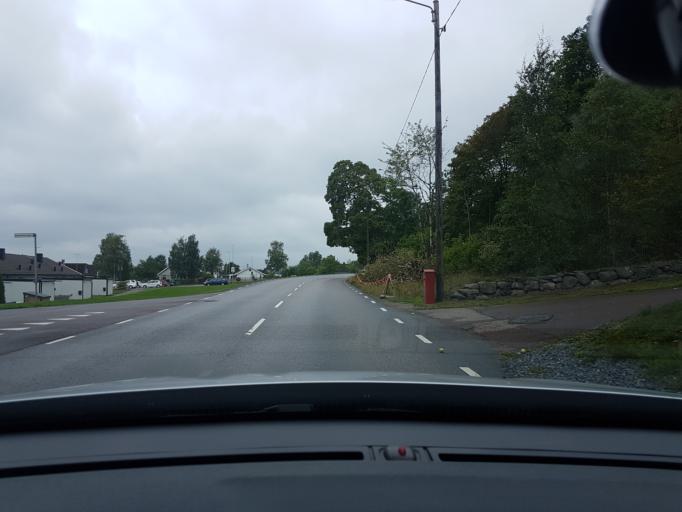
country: SE
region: Vaestra Goetaland
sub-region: Ale Kommun
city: Salanda
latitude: 57.9844
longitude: 12.2129
